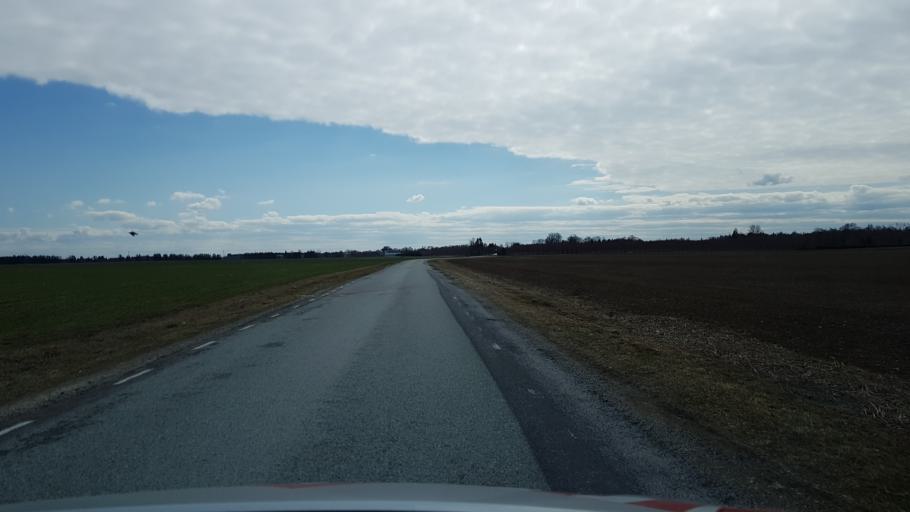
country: EE
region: Laeaene-Virumaa
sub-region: Haljala vald
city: Haljala
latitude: 59.4103
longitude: 26.2556
